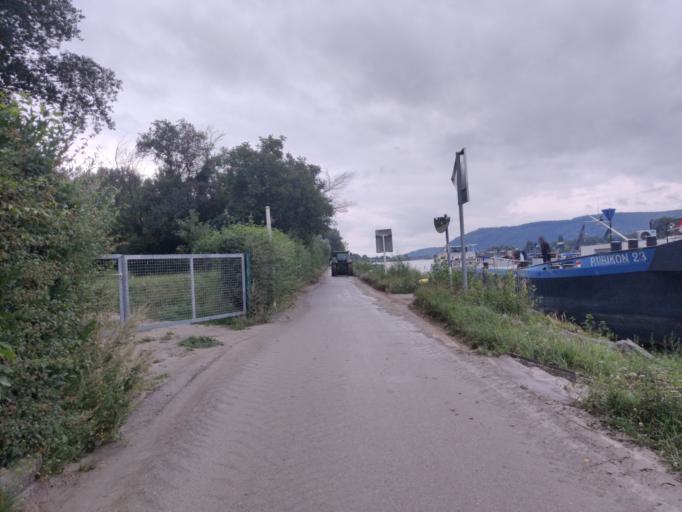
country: AT
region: Lower Austria
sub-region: Politischer Bezirk Korneuburg
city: Bisamberg
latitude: 48.3228
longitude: 16.3373
